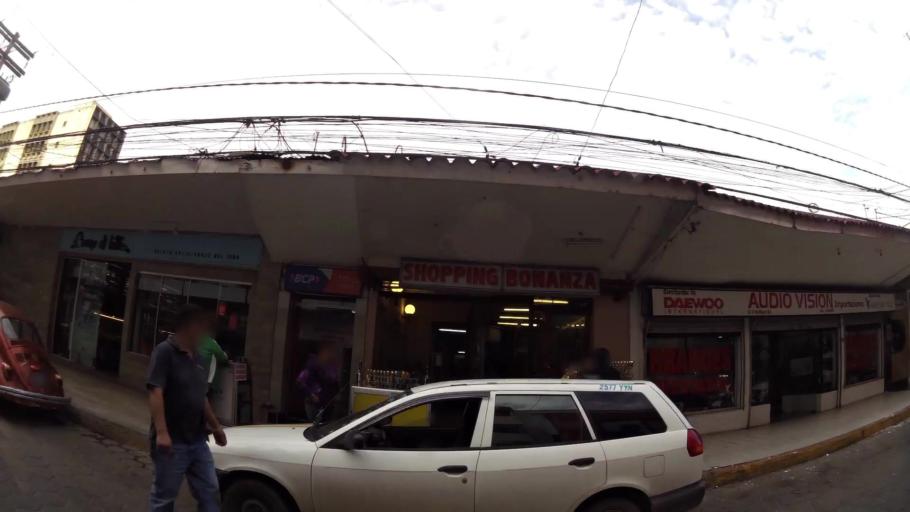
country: BO
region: Santa Cruz
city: Santa Cruz de la Sierra
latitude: -17.7833
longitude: -63.1837
